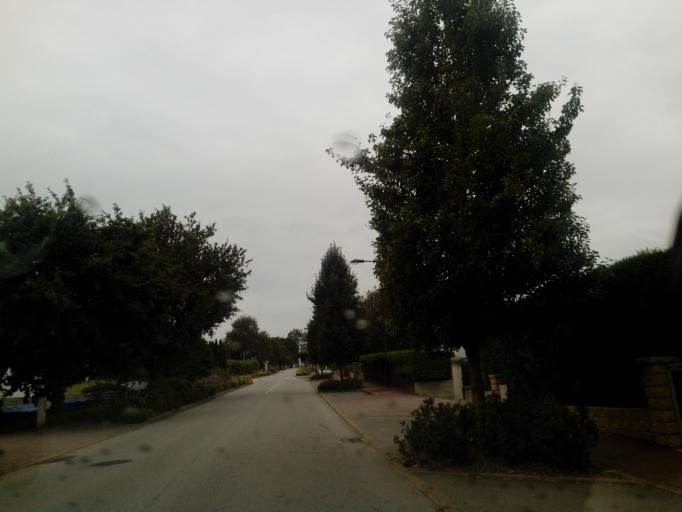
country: FR
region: Brittany
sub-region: Departement du Finistere
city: Tremeven
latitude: 47.8999
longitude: -3.5224
